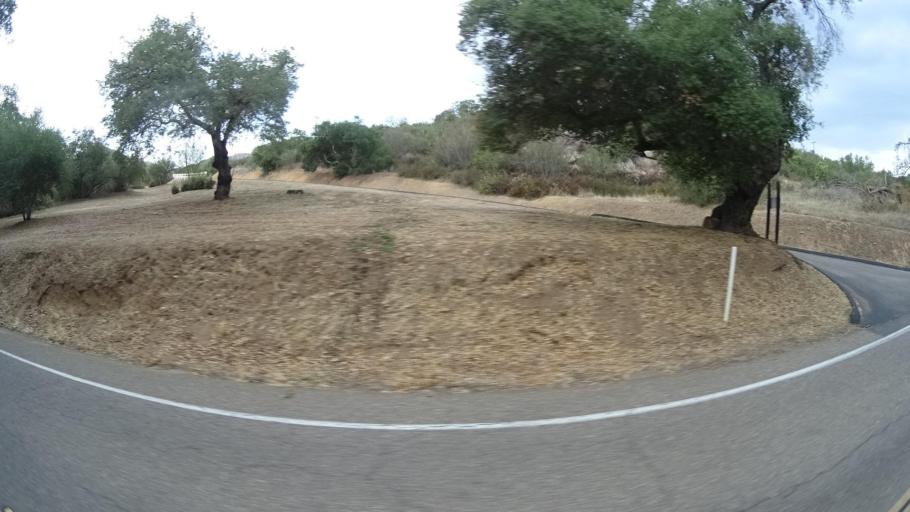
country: US
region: California
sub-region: San Diego County
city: Ramona
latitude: 32.9966
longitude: -116.9300
